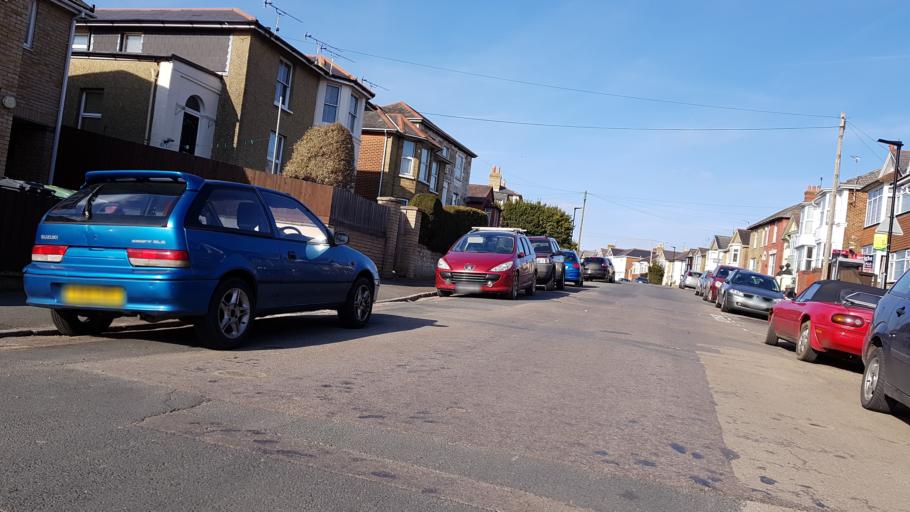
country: GB
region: England
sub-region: Isle of Wight
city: Ryde
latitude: 50.7251
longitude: -1.1566
